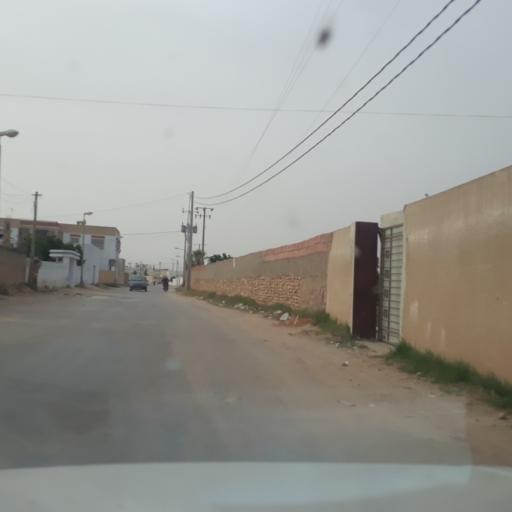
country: TN
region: Safaqis
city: Al Qarmadah
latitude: 34.8181
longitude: 10.7751
